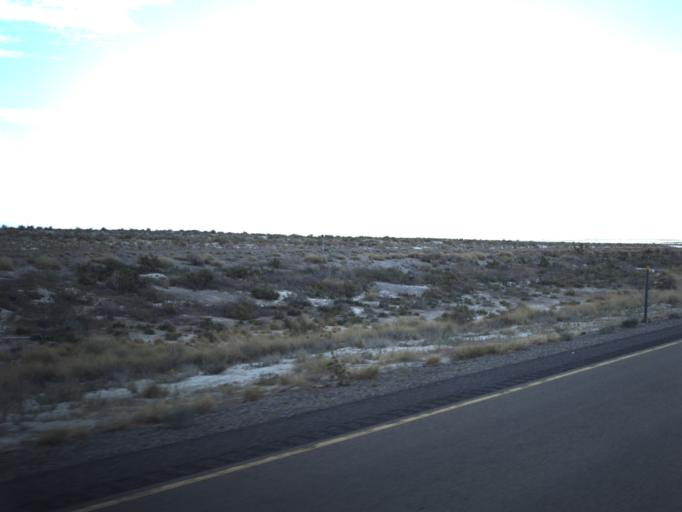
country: US
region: Utah
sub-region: Tooele County
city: Grantsville
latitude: 40.7571
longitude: -112.7672
